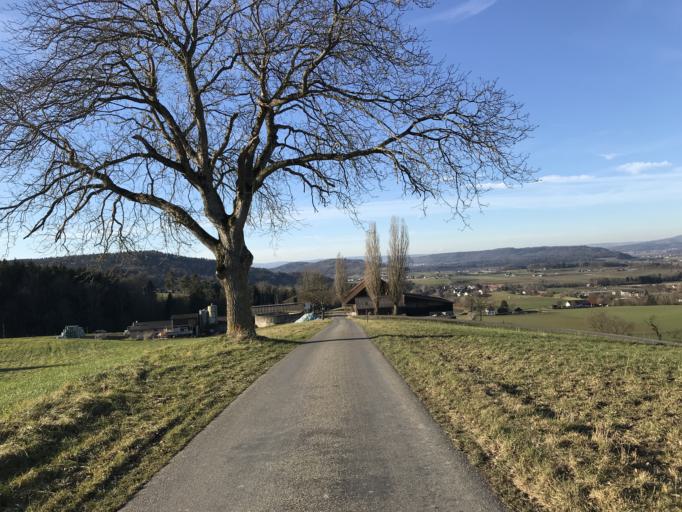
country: CH
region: Schaffhausen
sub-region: Bezirk Stein
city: Stein am Rhein
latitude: 47.6424
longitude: 8.8540
